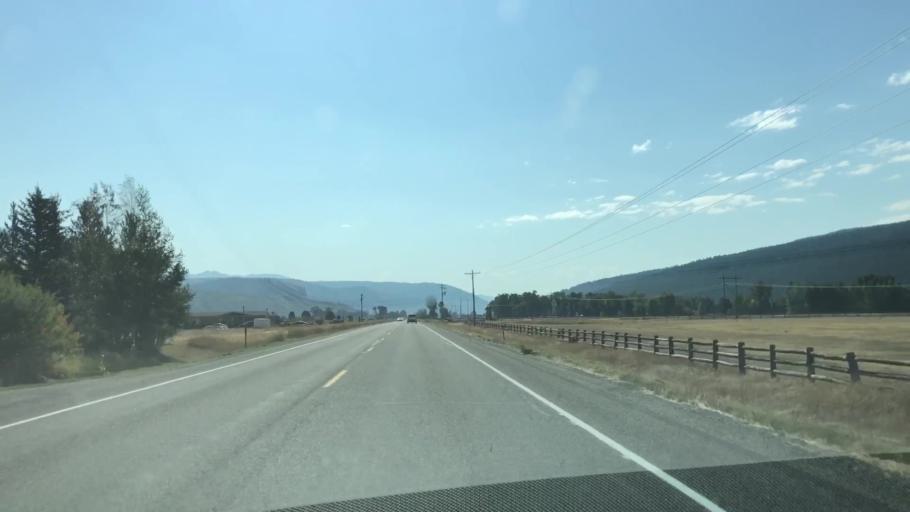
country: US
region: Idaho
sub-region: Teton County
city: Victor
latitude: 43.3980
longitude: -111.2825
